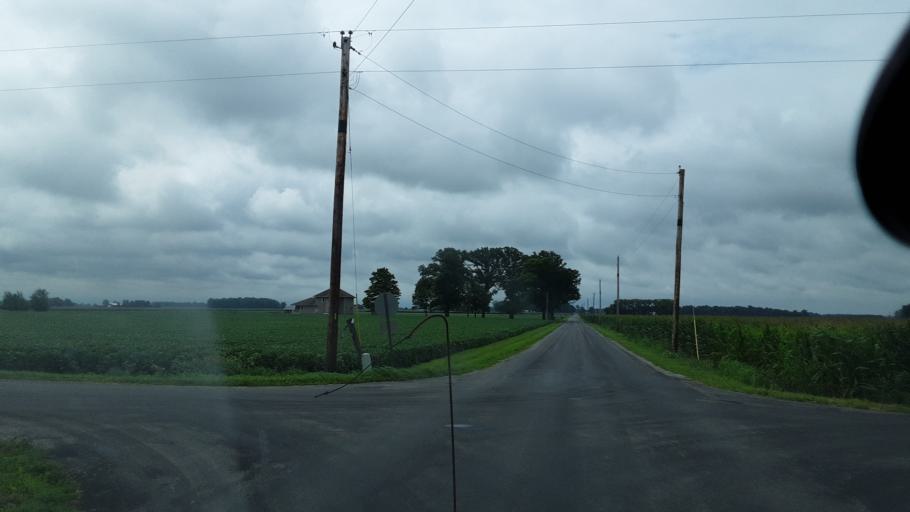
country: US
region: Indiana
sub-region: Wells County
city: Ossian
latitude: 40.8740
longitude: -85.1093
